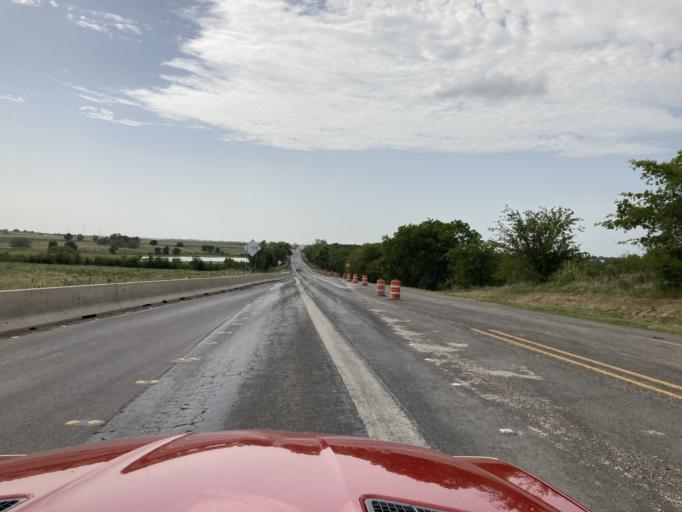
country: US
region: Texas
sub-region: Navarro County
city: Corsicana
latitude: 32.0516
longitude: -96.4224
